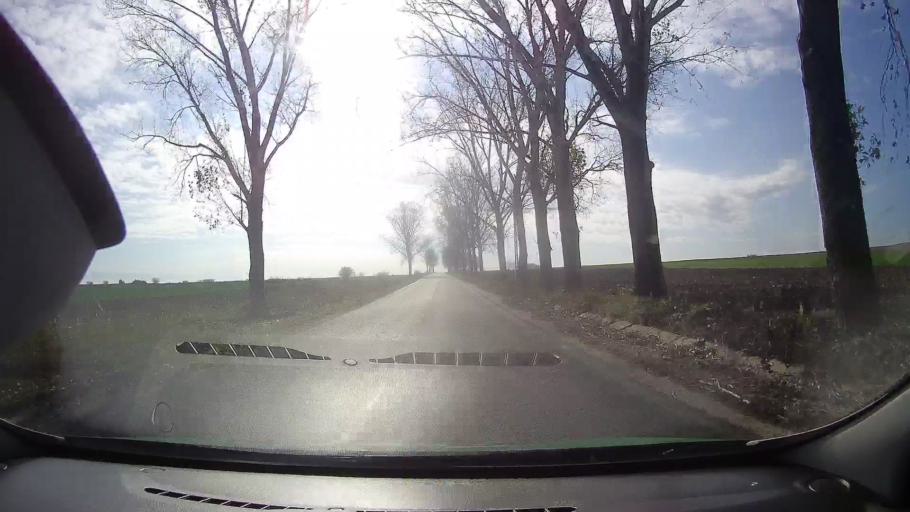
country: RO
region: Tulcea
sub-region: Comuna Valea Nucarilor
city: Agighiol
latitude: 45.0007
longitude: 28.8860
